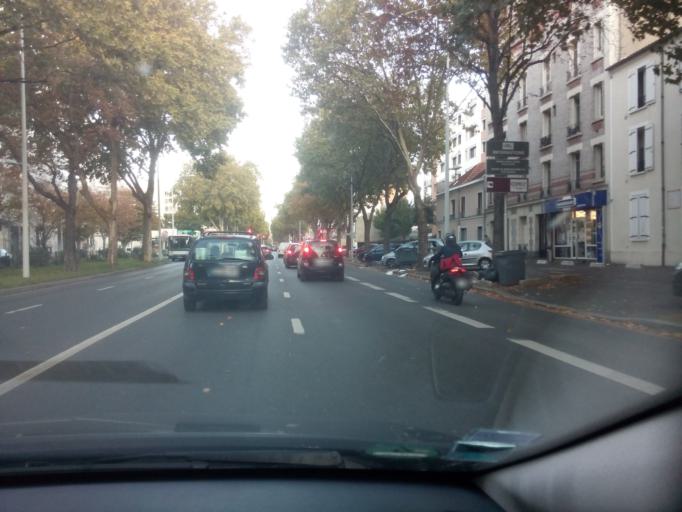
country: FR
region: Ile-de-France
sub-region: Departement des Hauts-de-Seine
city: Nanterre
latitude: 48.8858
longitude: 2.2172
